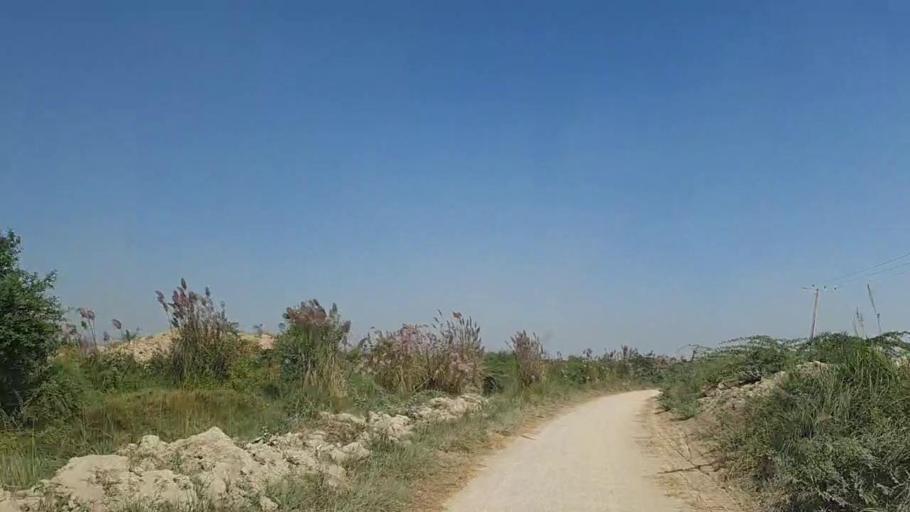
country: PK
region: Sindh
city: Daro Mehar
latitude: 24.7860
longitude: 68.1635
